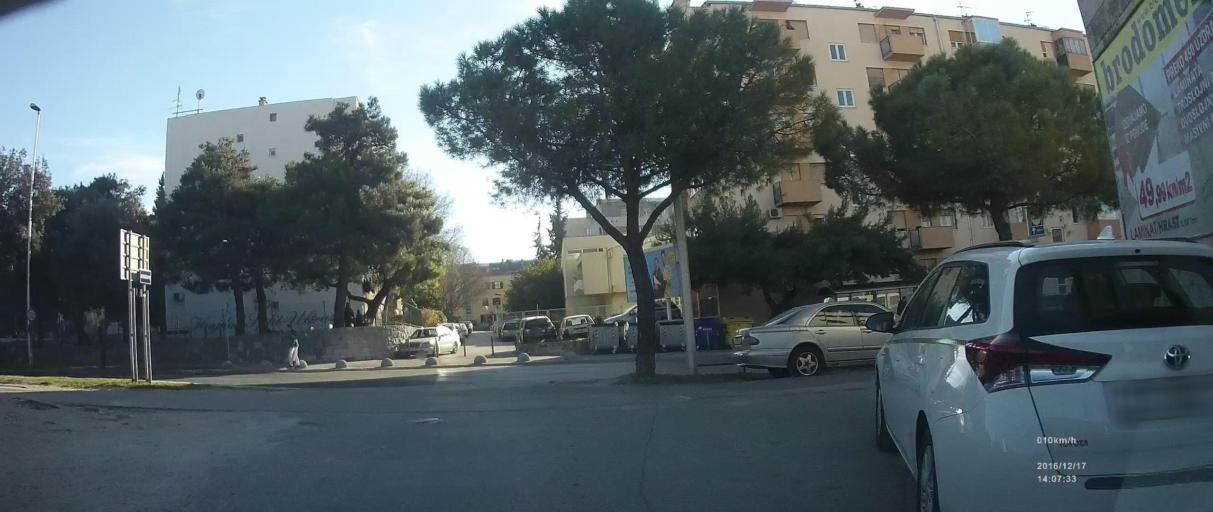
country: HR
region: Splitsko-Dalmatinska
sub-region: Grad Split
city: Split
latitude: 43.5187
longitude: 16.4361
